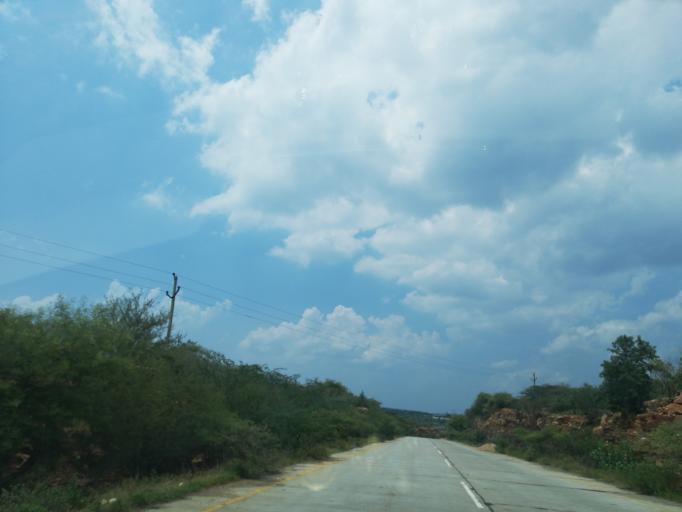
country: IN
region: Andhra Pradesh
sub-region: Guntur
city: Macherla
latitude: 16.5704
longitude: 79.3322
